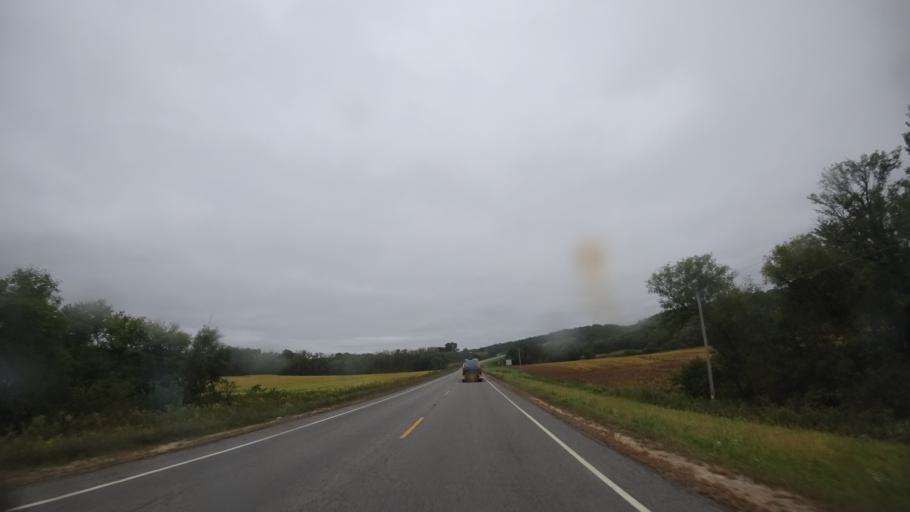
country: US
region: Wisconsin
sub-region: Crawford County
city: Prairie du Chien
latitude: 43.0309
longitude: -91.0011
